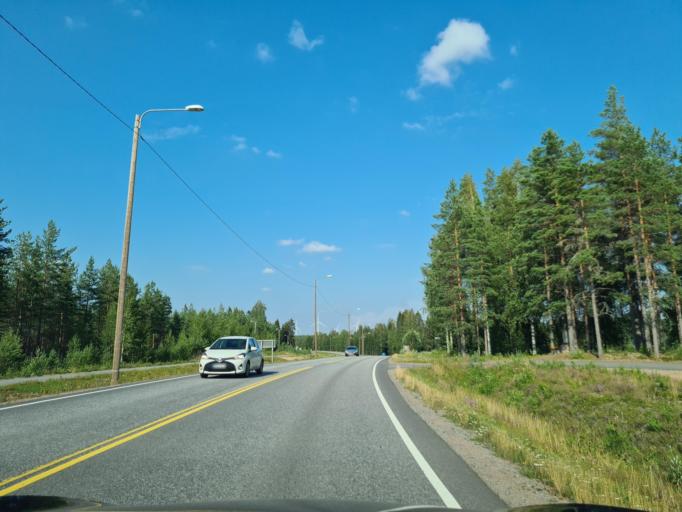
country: FI
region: Satakunta
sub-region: Pohjois-Satakunta
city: Karvia
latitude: 62.0750
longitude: 22.5080
